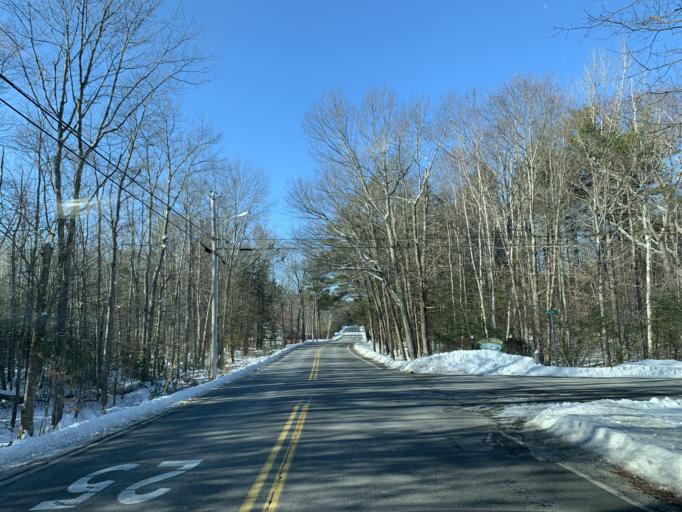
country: US
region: Maine
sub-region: York County
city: Ogunquit
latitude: 43.2476
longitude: -70.6146
